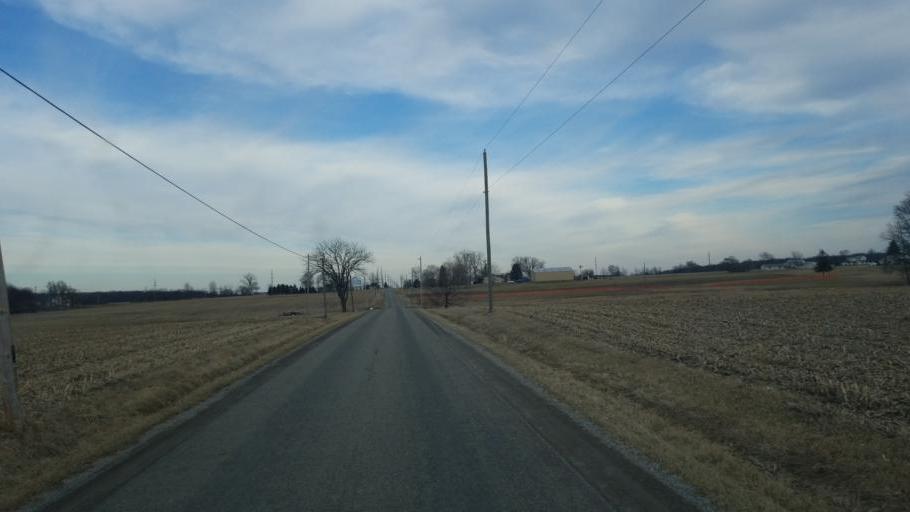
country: US
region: Ohio
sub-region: Defiance County
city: Hicksville
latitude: 41.3535
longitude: -84.7734
